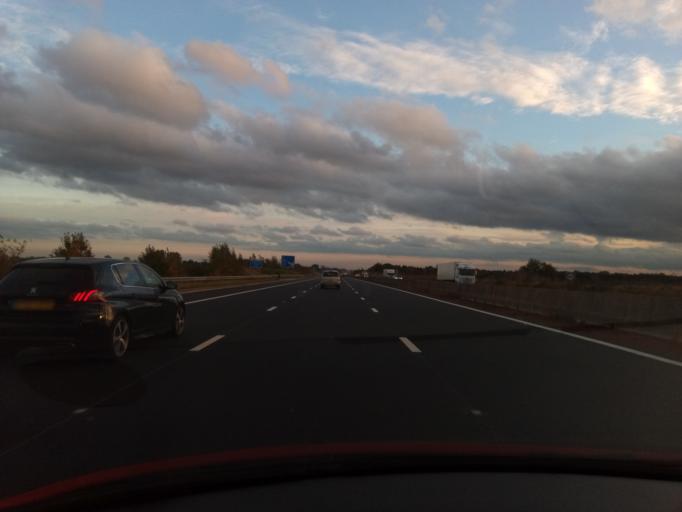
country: GB
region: England
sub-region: North Yorkshire
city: Ripon
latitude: 54.2016
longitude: -1.4712
